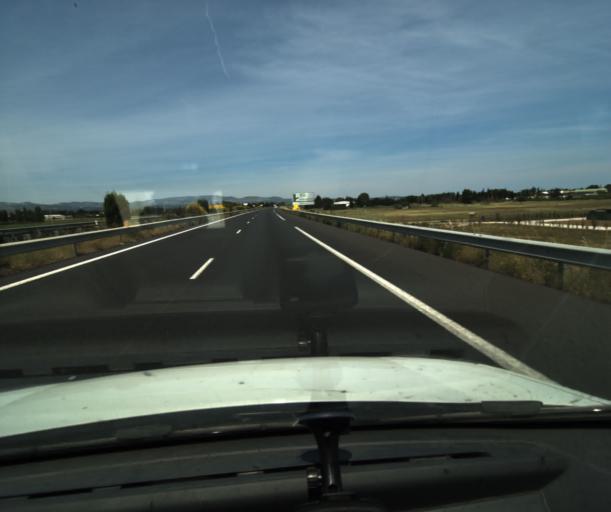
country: FR
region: Languedoc-Roussillon
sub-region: Departement des Pyrenees-Orientales
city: Rivesaltes
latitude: 42.7624
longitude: 2.8919
